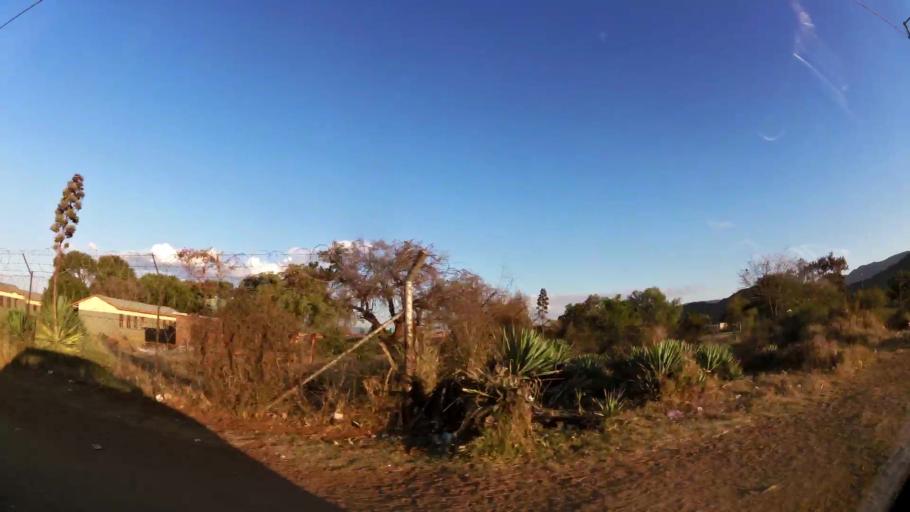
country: ZA
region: Limpopo
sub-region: Waterberg District Municipality
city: Mokopane
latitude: -24.1413
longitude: 28.9786
